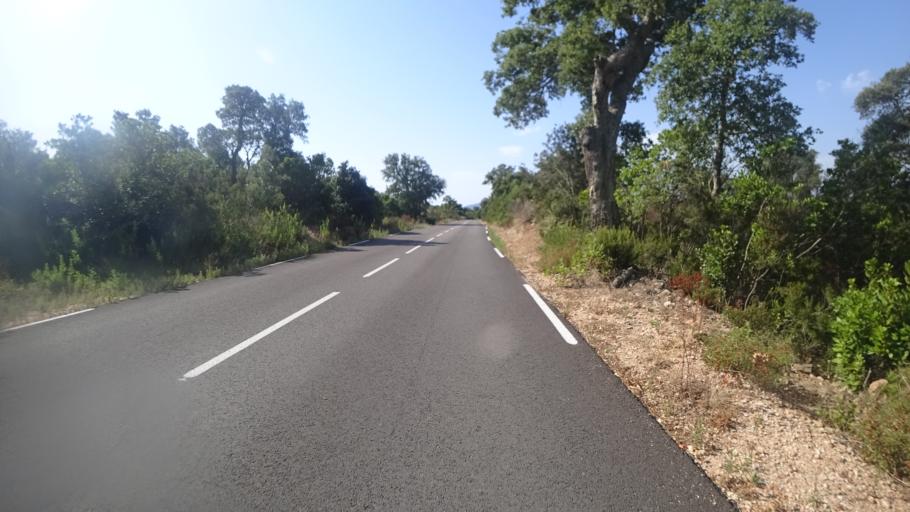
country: FR
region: Corsica
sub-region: Departement de la Corse-du-Sud
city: Porto-Vecchio
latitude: 41.6566
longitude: 9.3256
